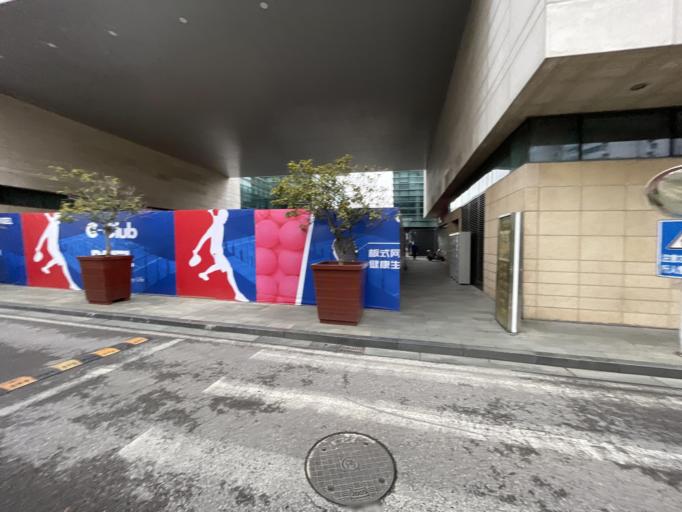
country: CN
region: Shanghai Shi
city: Yangpu
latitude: 31.3067
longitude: 121.5100
